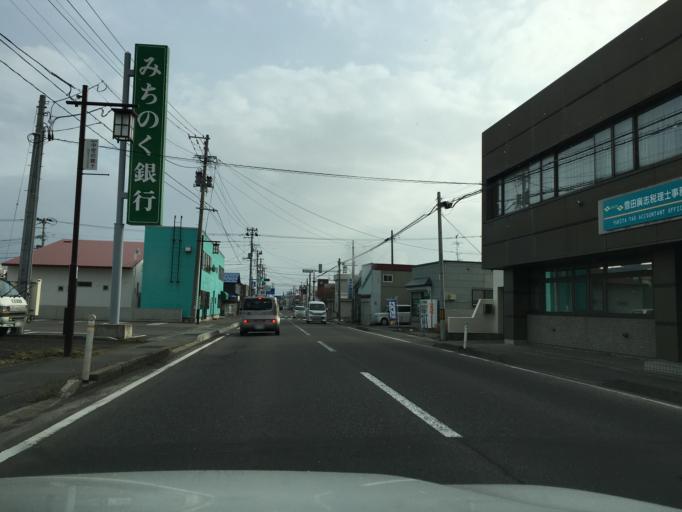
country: JP
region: Aomori
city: Namioka
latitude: 40.7136
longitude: 140.5907
